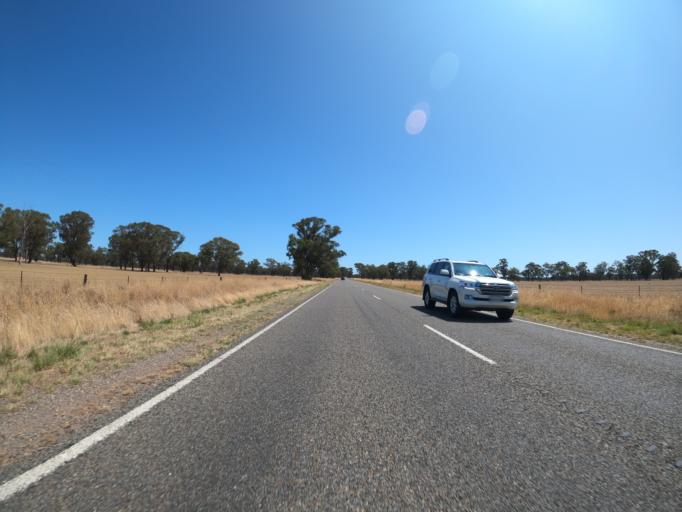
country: AU
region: New South Wales
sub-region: Corowa Shire
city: Corowa
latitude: -36.0813
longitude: 146.3378
